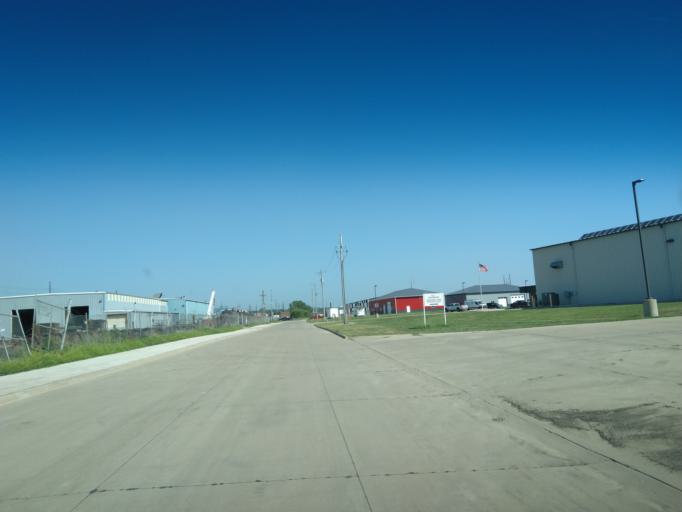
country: US
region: Iowa
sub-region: Woodbury County
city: Sioux City
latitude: 42.4807
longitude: -96.3854
